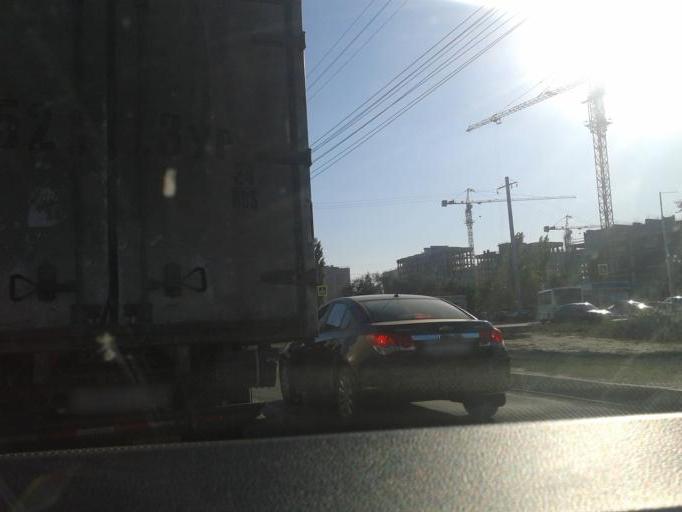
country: RU
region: Volgograd
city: Volgograd
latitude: 48.6266
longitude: 44.4266
